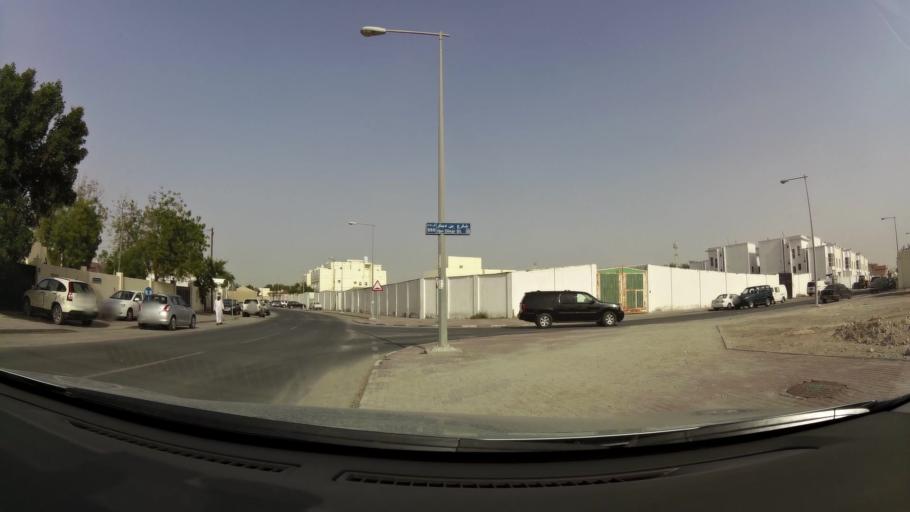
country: QA
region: Baladiyat ar Rayyan
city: Ar Rayyan
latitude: 25.2368
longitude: 51.4392
